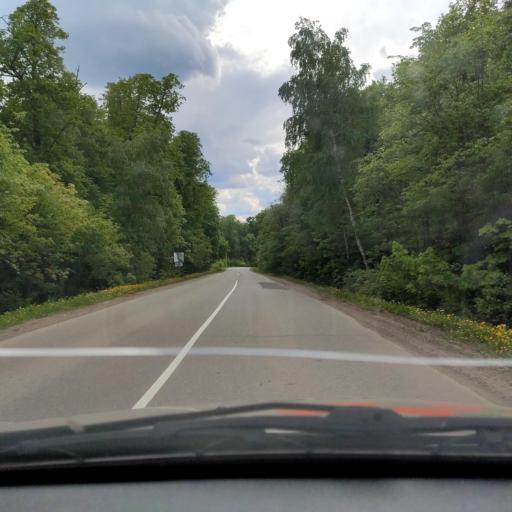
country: RU
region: Bashkortostan
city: Avdon
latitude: 54.6542
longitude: 55.7000
